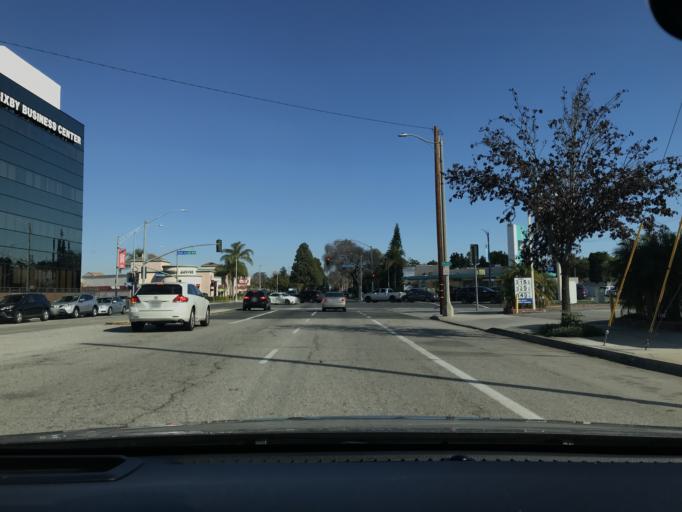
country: US
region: California
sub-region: Los Angeles County
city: Signal Hill
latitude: 33.8364
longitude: -118.1856
